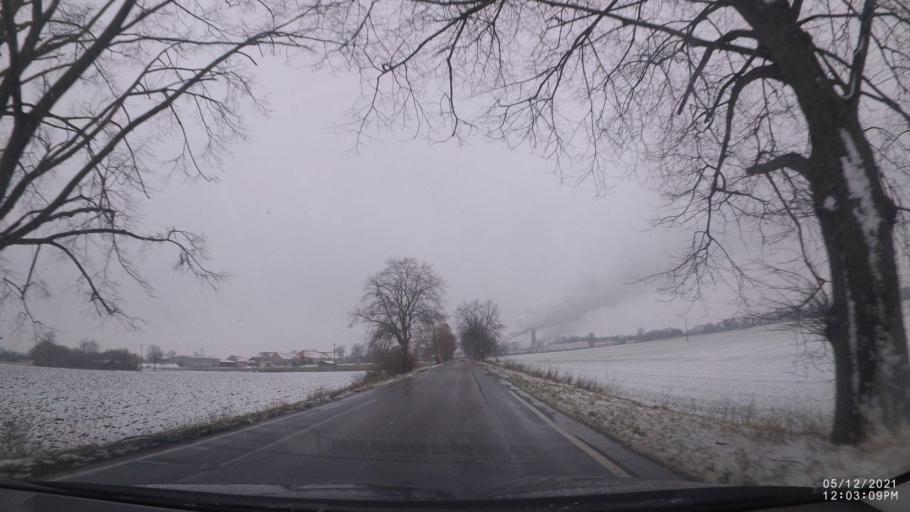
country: CZ
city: Ceske Mezirici
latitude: 50.2819
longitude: 16.0646
